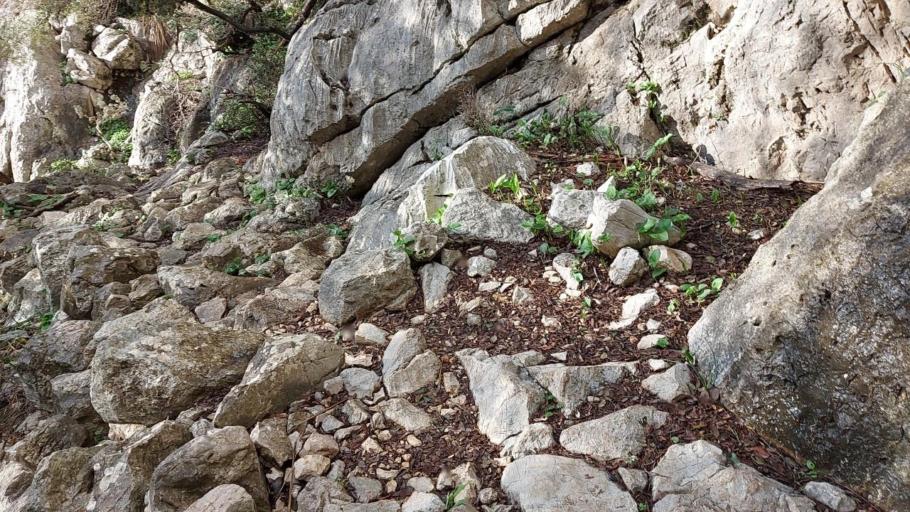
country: ES
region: Balearic Islands
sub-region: Illes Balears
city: Alaro
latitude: 39.7291
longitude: 2.7733
